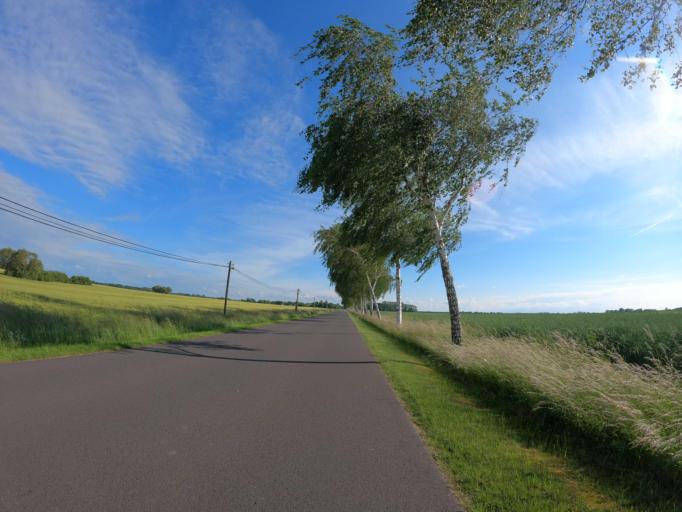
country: DE
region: Mecklenburg-Vorpommern
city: Preetz
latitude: 54.3411
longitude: 12.9731
